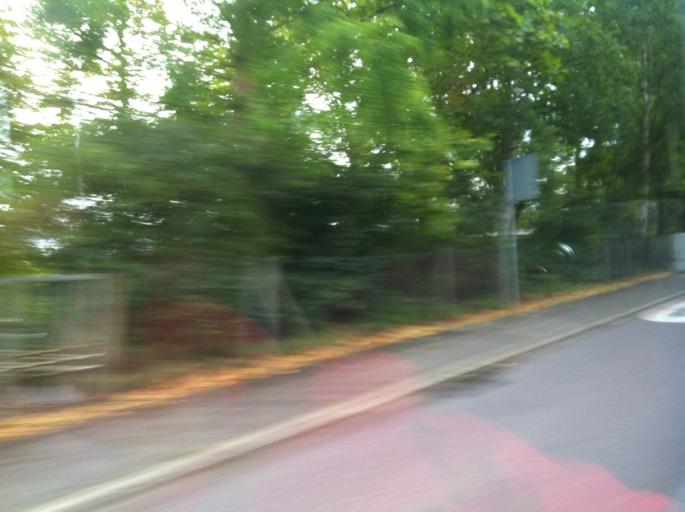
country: DE
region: North Rhine-Westphalia
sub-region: Regierungsbezirk Koln
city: Konigswinter
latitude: 50.7034
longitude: 7.1506
